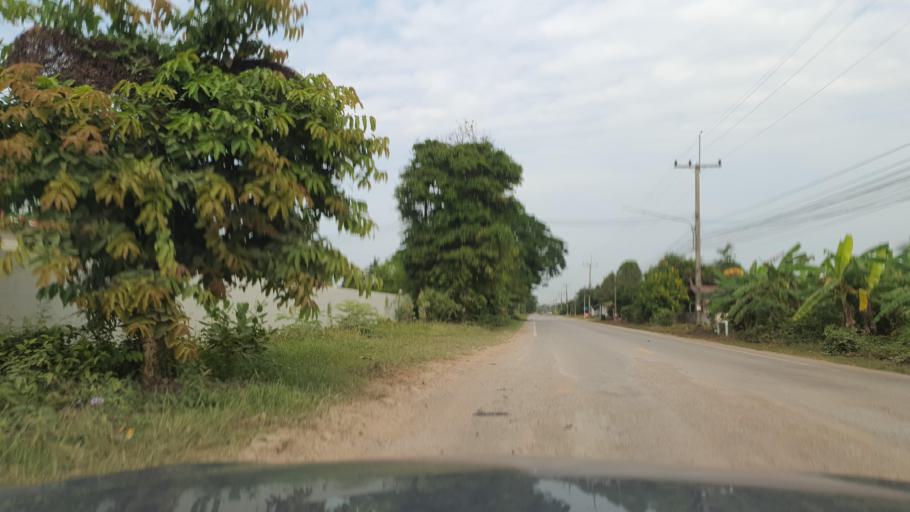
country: TH
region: Phitsanulok
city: Bang Rakam
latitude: 16.8147
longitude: 100.1758
